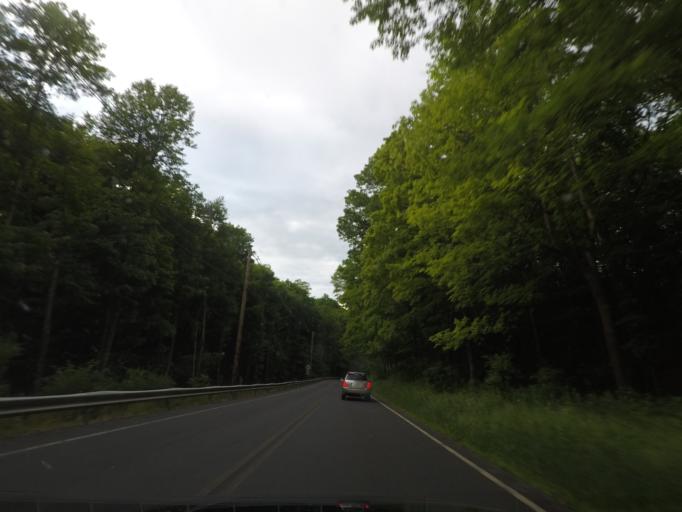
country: US
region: New York
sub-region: Dutchess County
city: Pine Plains
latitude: 41.9918
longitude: -73.6906
